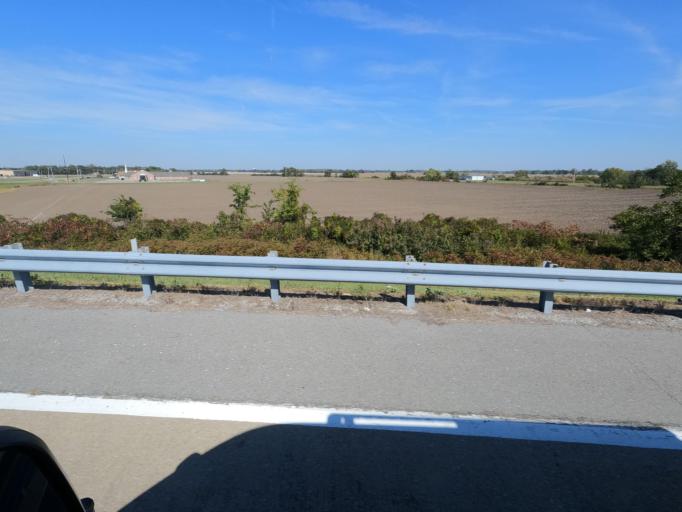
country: US
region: Missouri
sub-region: Pemiscot County
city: Caruthersville
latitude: 36.1521
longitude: -89.6626
